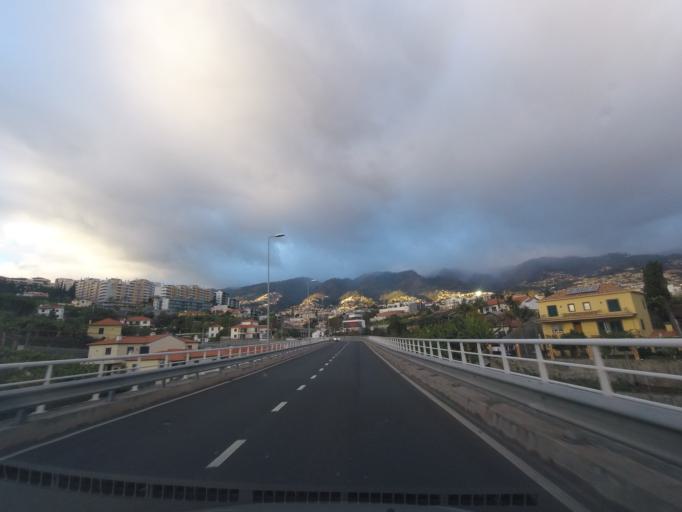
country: PT
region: Madeira
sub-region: Funchal
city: Nossa Senhora do Monte
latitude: 32.6520
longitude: -16.9286
